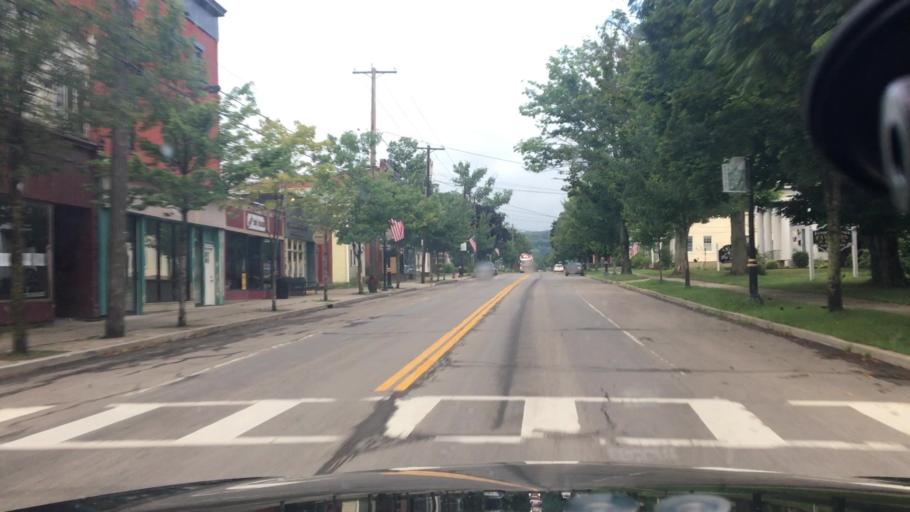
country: US
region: New York
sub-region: Cattaraugus County
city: Randolph
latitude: 42.1619
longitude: -78.9765
